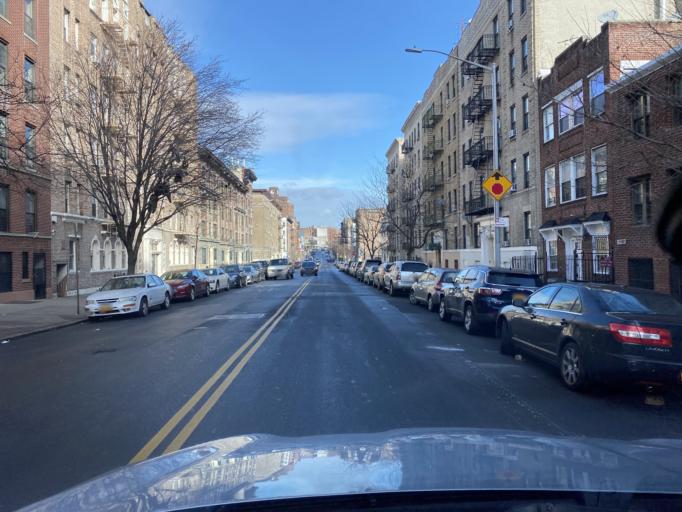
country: US
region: New York
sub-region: New York County
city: Inwood
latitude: 40.8590
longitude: -73.8972
